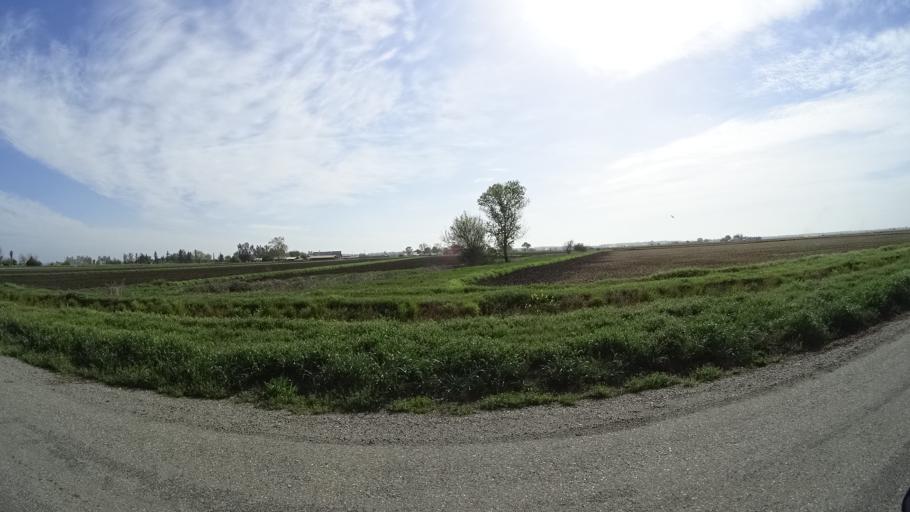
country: US
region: California
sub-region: Glenn County
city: Willows
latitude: 39.5779
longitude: -122.0466
